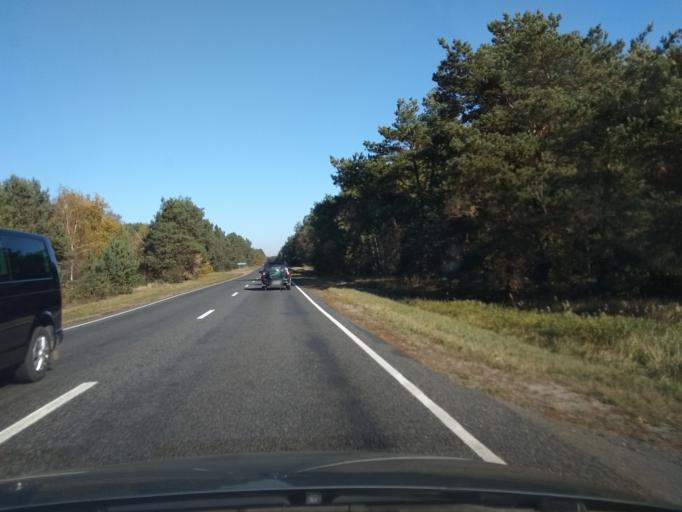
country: BY
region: Brest
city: Kobryn
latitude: 52.1347
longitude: 24.3076
